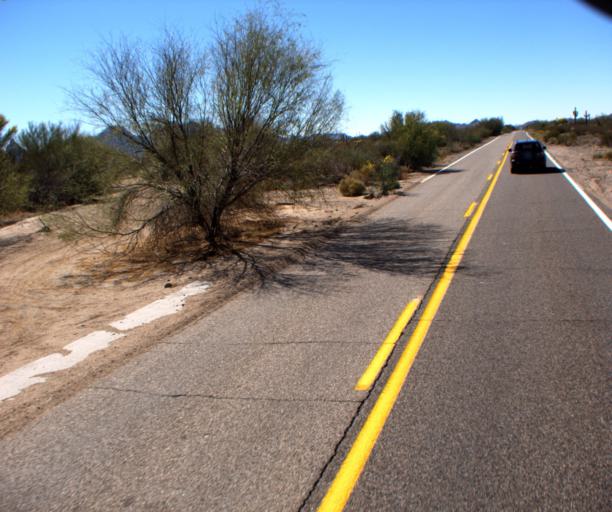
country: US
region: Arizona
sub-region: Pima County
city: Ajo
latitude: 32.1732
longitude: -112.7626
